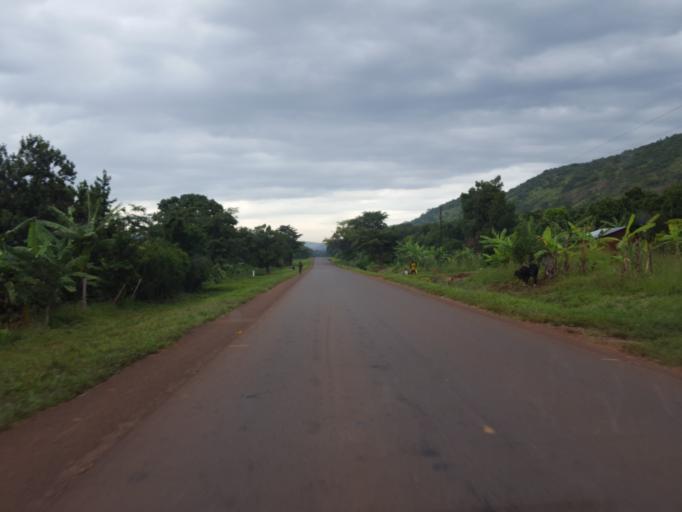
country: UG
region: Central Region
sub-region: Kiboga District
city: Kiboga
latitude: 0.8447
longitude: 31.8781
